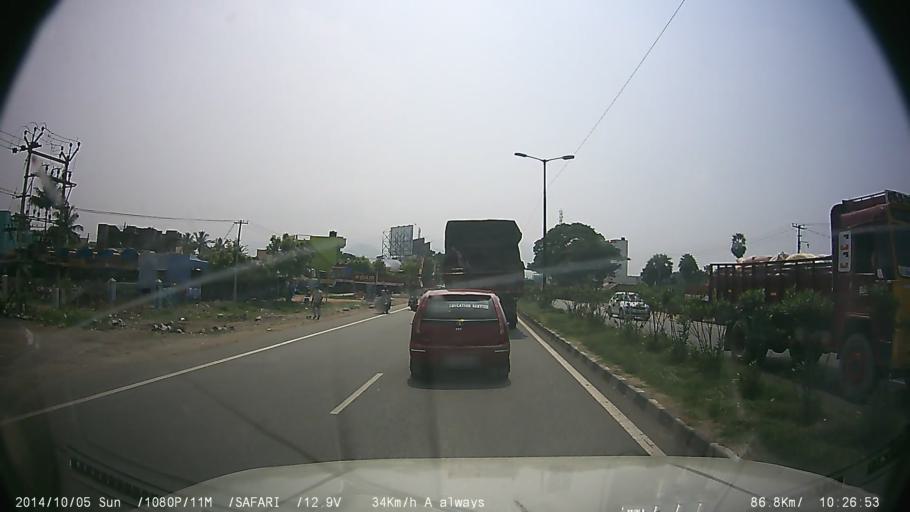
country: IN
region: Tamil Nadu
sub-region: Salem
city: Salem
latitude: 11.6346
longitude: 78.1248
